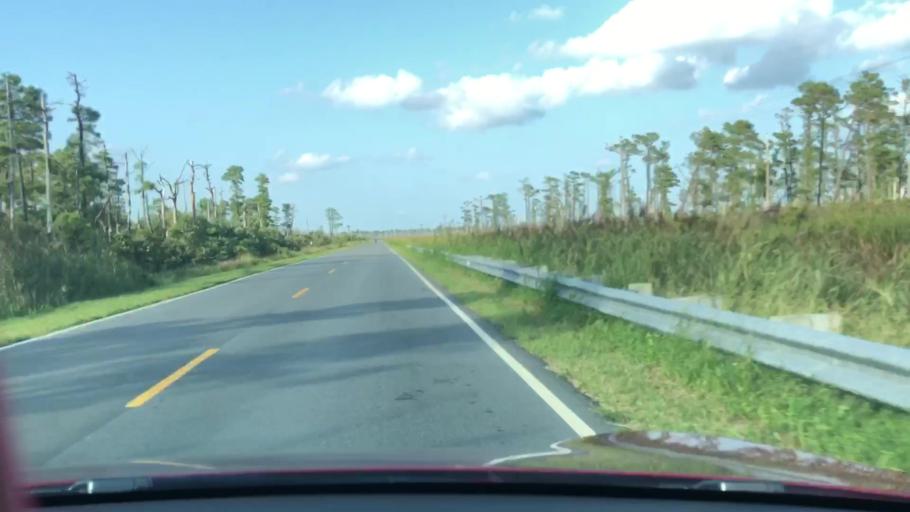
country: US
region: North Carolina
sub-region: Dare County
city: Wanchese
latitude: 35.6154
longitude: -75.7933
